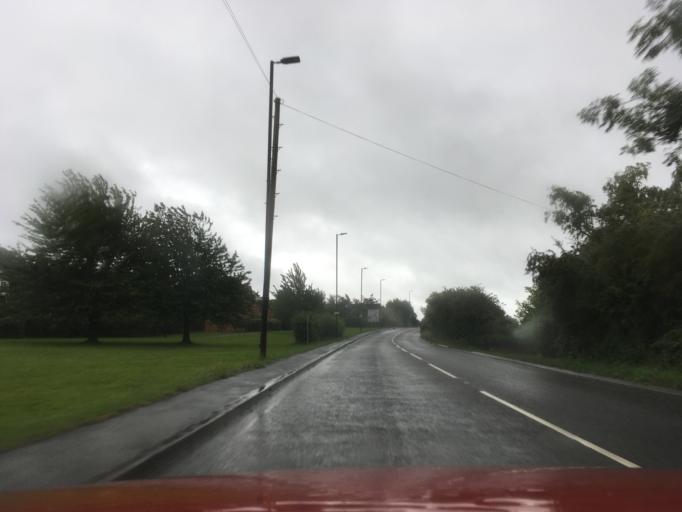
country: GB
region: England
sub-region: Gloucestershire
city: Tewkesbury
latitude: 51.9795
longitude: -2.1550
